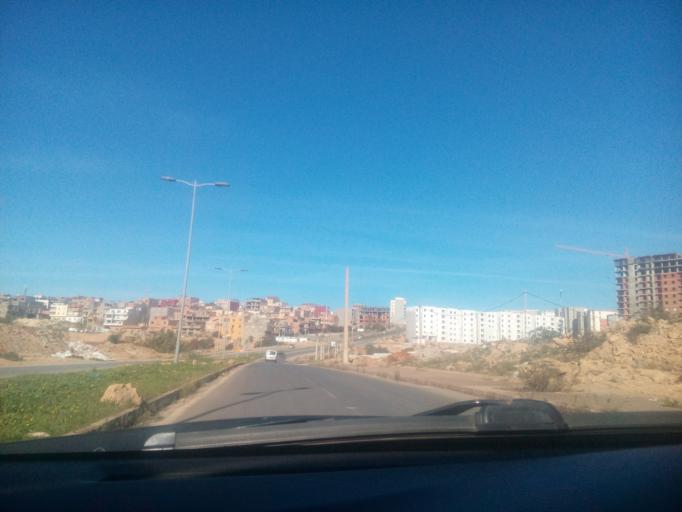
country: DZ
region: Oran
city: Bir el Djir
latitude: 35.7414
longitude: -0.5471
